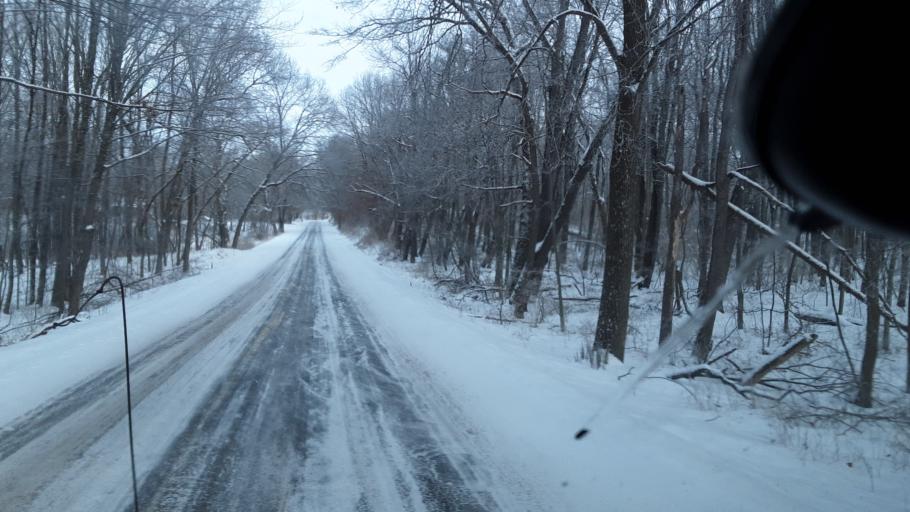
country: US
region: Michigan
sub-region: Ingham County
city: Leslie
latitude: 42.3642
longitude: -84.4826
